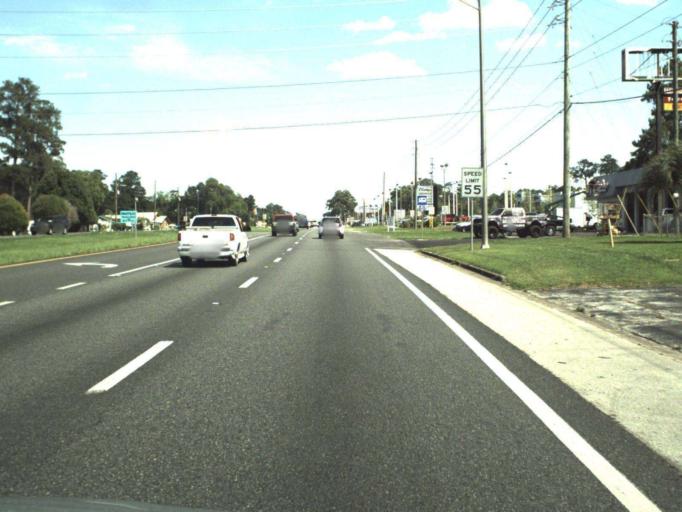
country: US
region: Florida
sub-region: Marion County
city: Ocala
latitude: 29.1547
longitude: -82.1268
